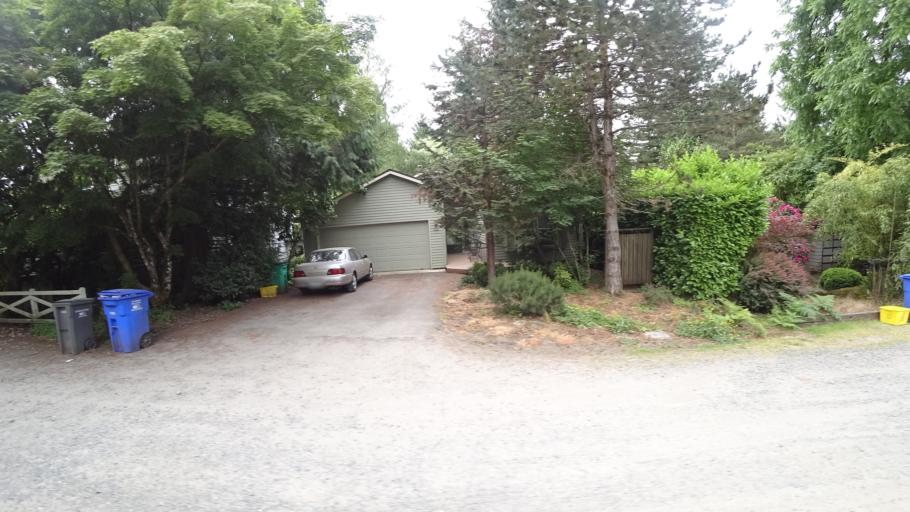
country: US
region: Oregon
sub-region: Clackamas County
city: Lake Oswego
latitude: 45.4619
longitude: -122.6884
